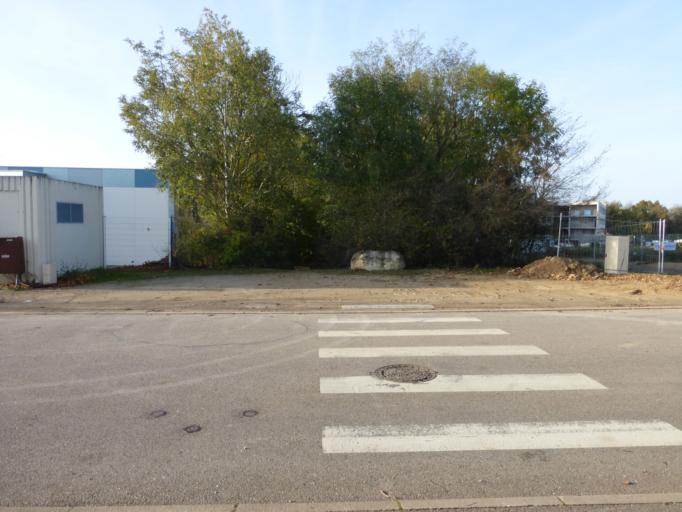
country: FR
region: Lorraine
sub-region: Departement de Meurthe-et-Moselle
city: Laxou
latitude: 48.7041
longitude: 6.1282
